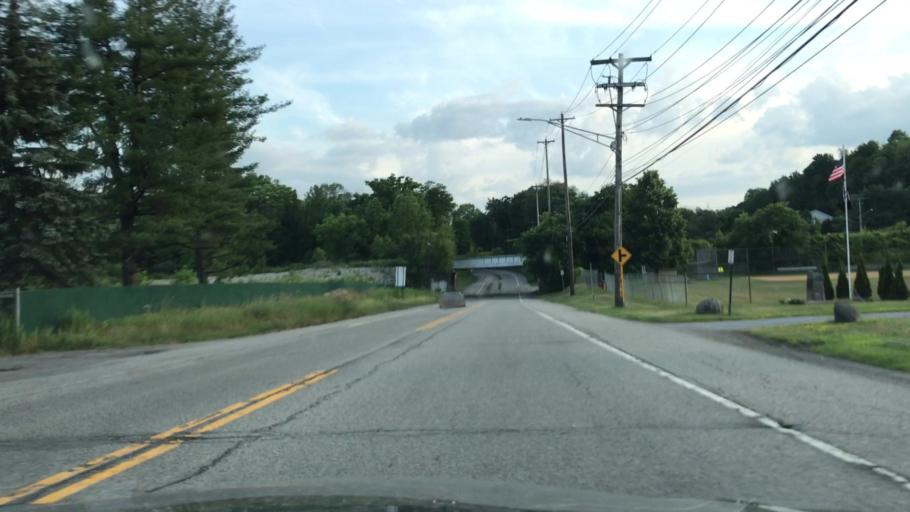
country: US
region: New York
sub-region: Orange County
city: Harriman
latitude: 41.3097
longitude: -74.1434
